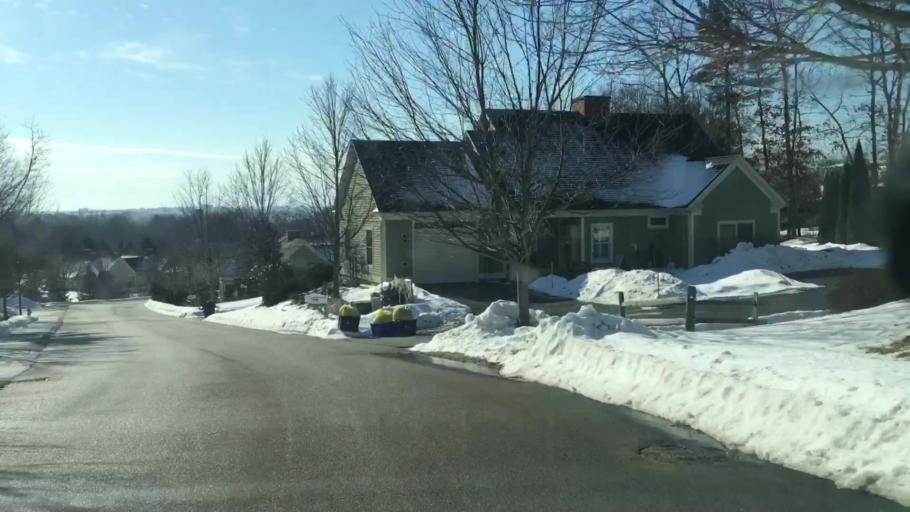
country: US
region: Maine
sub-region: Cumberland County
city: Falmouth
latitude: 43.7226
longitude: -70.2493
